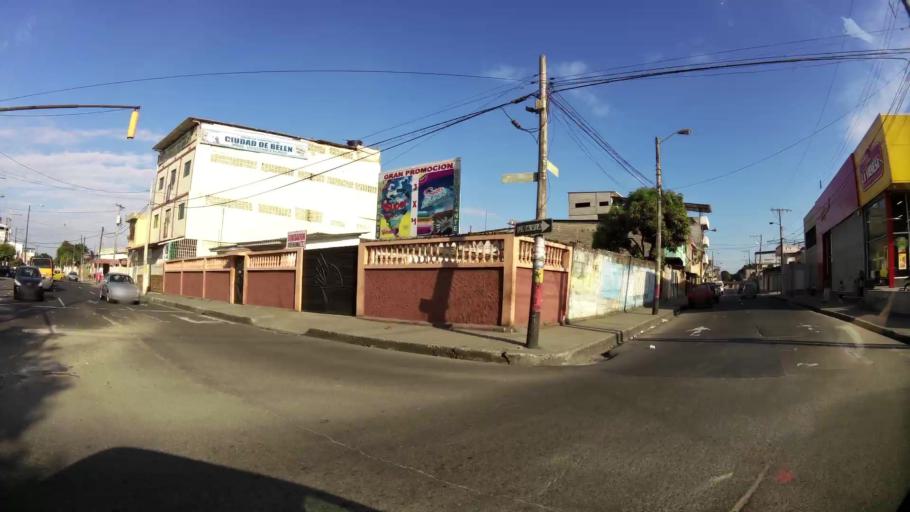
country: EC
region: Guayas
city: Guayaquil
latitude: -2.2253
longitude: -79.9048
